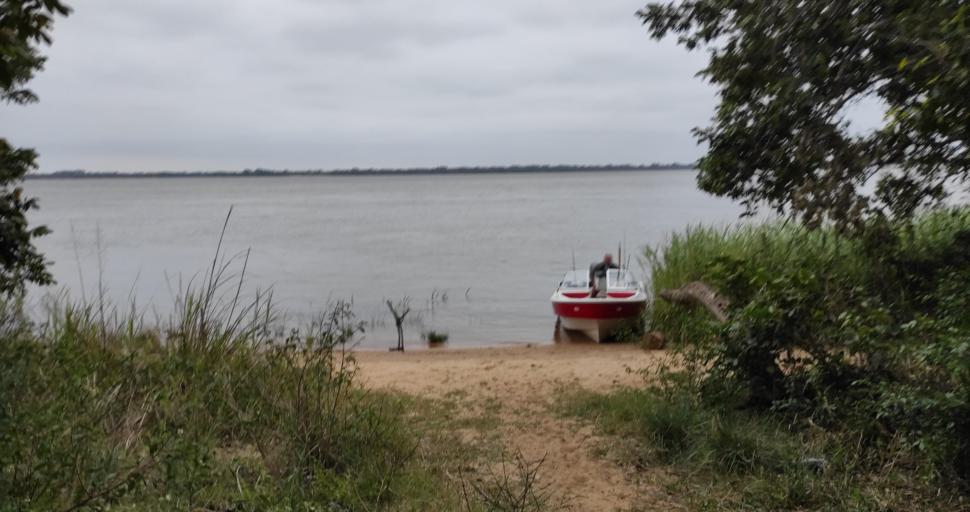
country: AR
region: Corrientes
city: Ituzaingo
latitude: -27.5928
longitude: -56.8010
